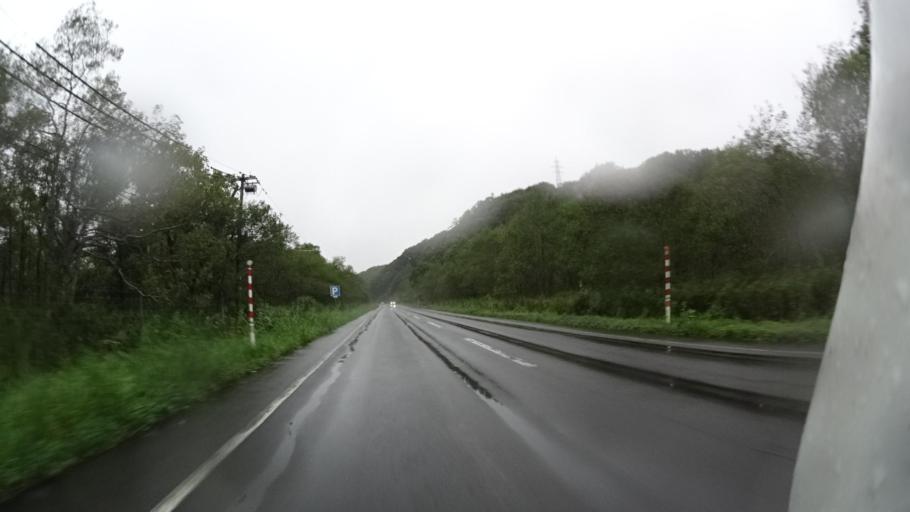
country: JP
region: Hokkaido
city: Kushiro
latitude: 43.0846
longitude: 144.8458
